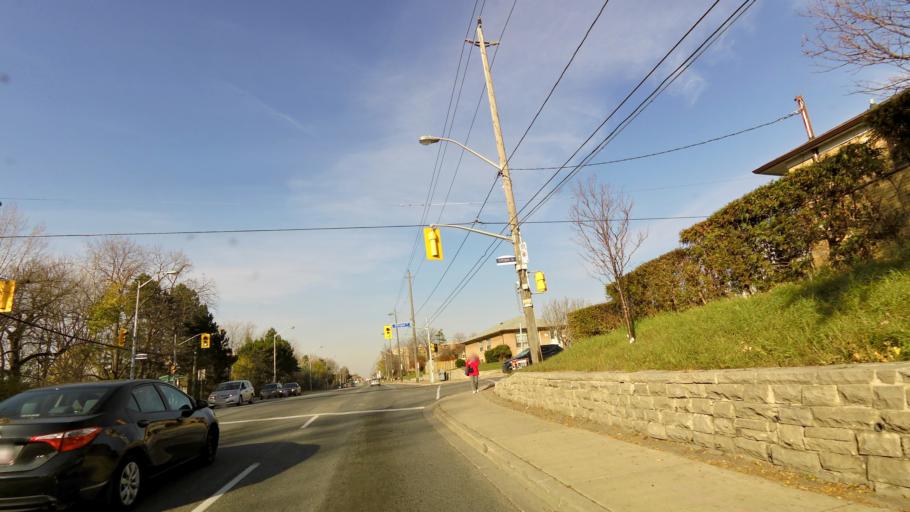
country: CA
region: Ontario
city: Concord
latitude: 43.7343
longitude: -79.5117
